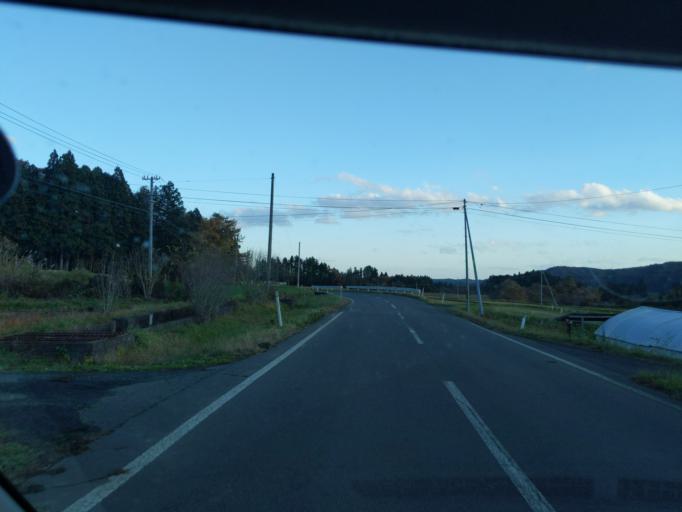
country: JP
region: Iwate
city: Mizusawa
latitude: 39.0483
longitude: 141.0504
